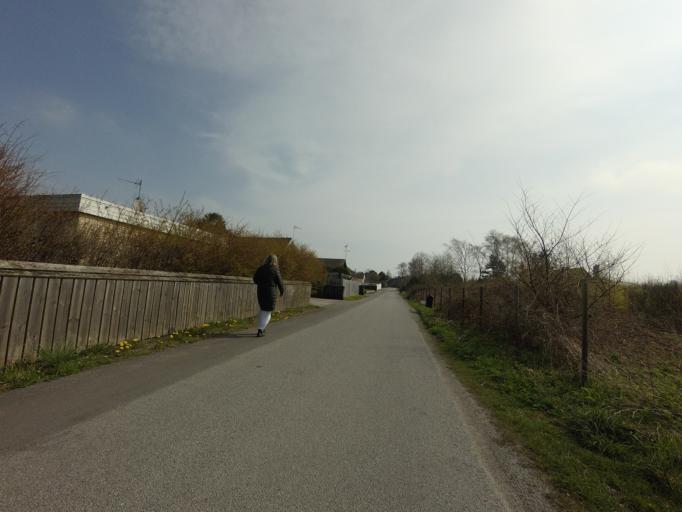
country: SE
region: Skane
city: Smygehamn
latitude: 55.3574
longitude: 13.4137
